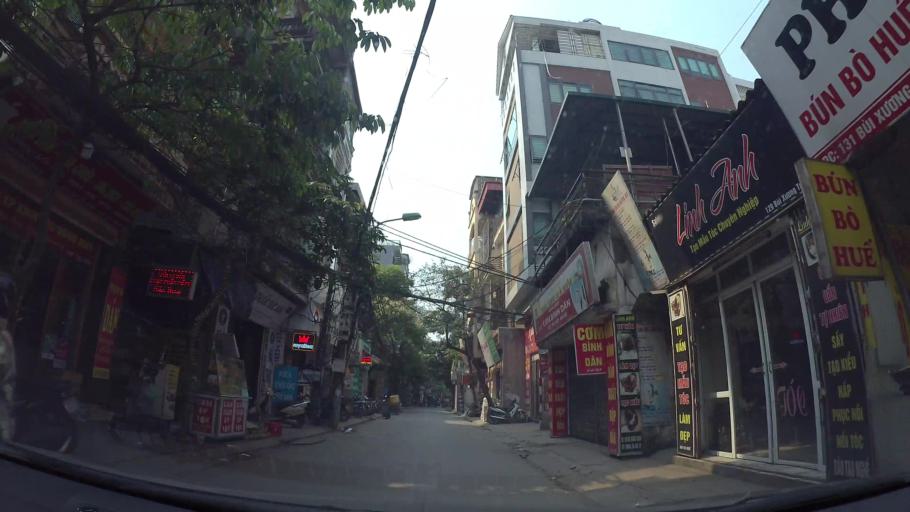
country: VN
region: Ha Noi
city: Thanh Xuan
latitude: 20.9887
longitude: 105.8181
